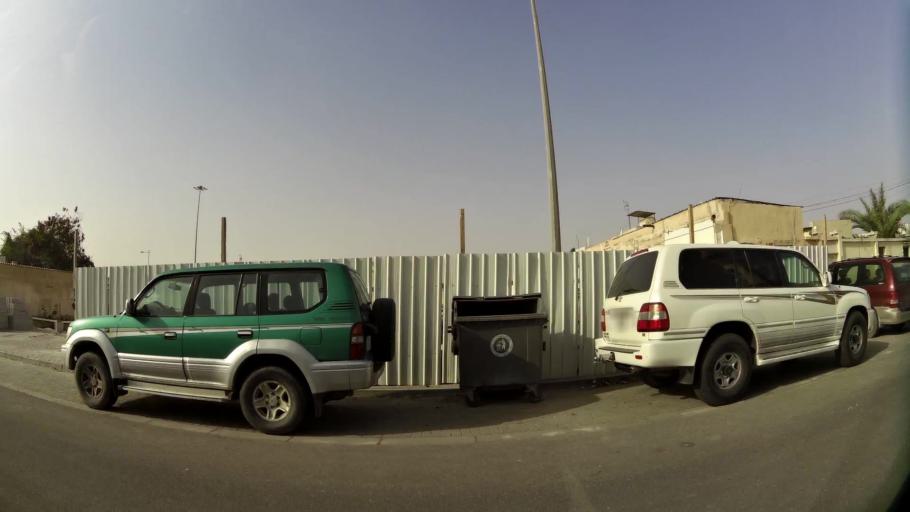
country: QA
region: Baladiyat ar Rayyan
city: Ar Rayyan
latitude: 25.2329
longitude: 51.4348
